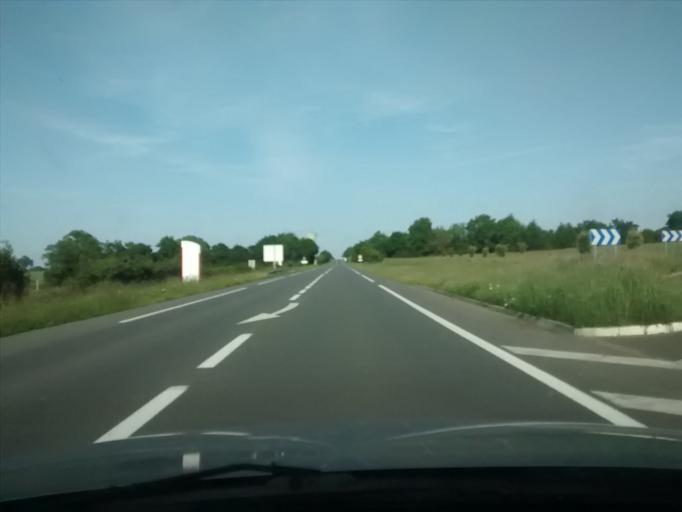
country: FR
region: Pays de la Loire
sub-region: Departement de la Mayenne
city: Vaiges
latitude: 48.0372
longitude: -0.4675
